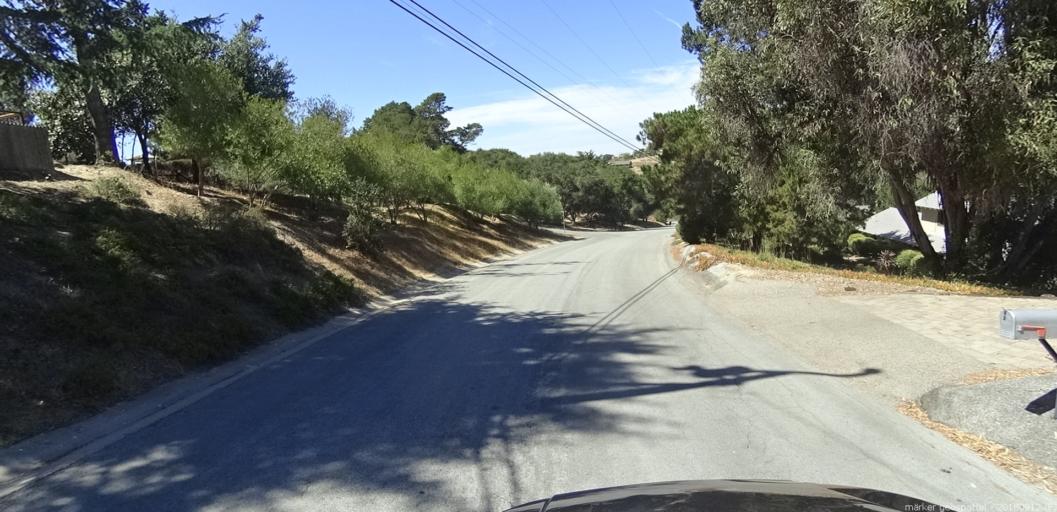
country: US
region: California
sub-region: Monterey County
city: Carmel Valley Village
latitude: 36.4943
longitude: -121.7348
